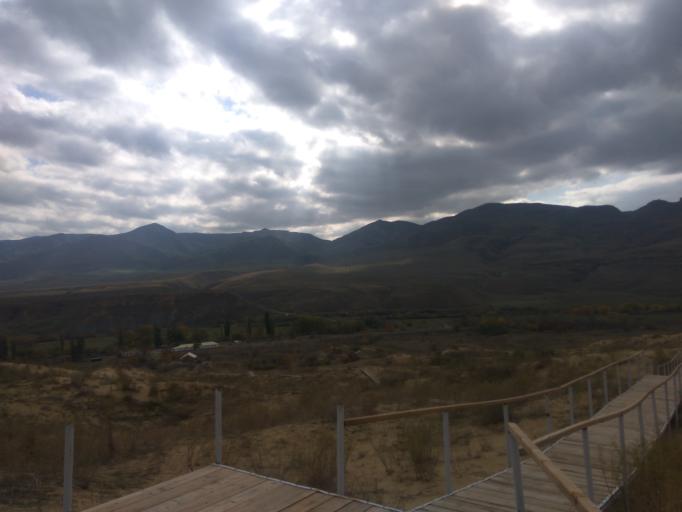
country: RU
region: Dagestan
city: Korkmaskala
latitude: 43.0073
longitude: 47.2345
